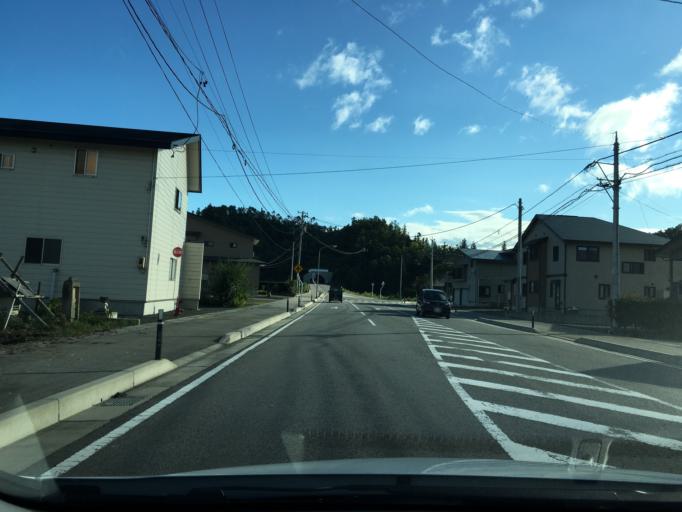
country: JP
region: Yamagata
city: Yonezawa
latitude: 37.9362
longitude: 140.1662
